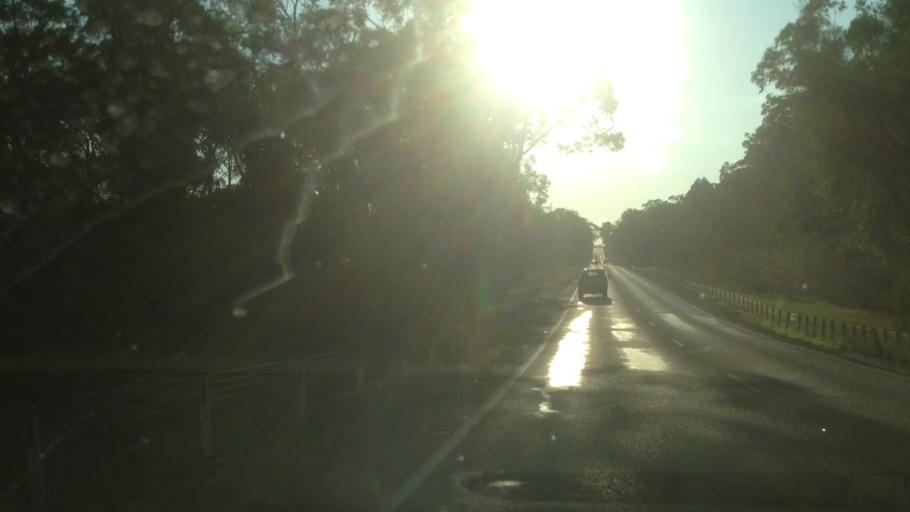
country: AU
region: New South Wales
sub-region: Cessnock
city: Kurri Kurri
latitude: -32.8294
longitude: 151.5003
